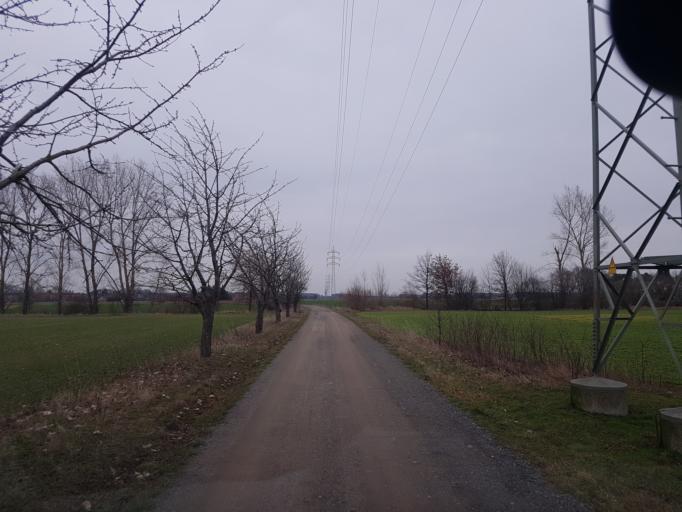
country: DE
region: Brandenburg
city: Falkenberg
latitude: 51.5685
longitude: 13.2363
